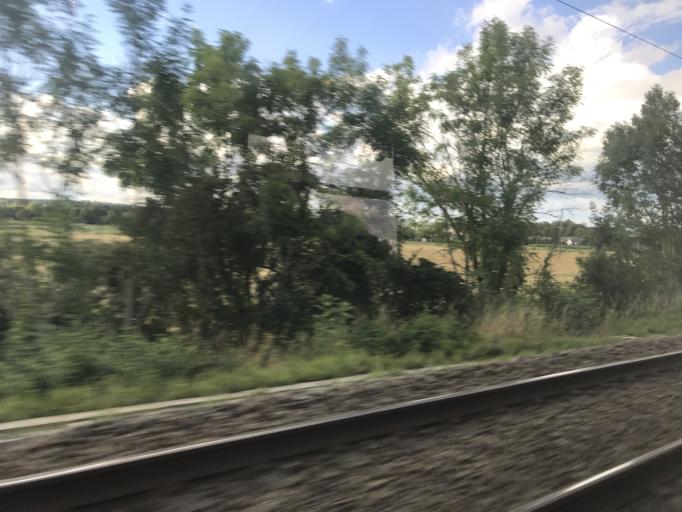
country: FR
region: Champagne-Ardenne
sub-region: Departement des Ardennes
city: Bazeilles
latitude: 49.6692
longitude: 4.9750
